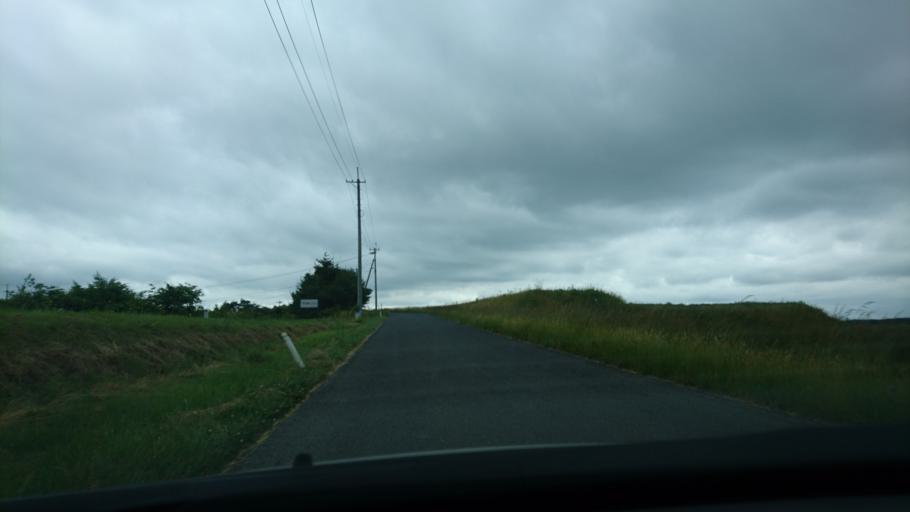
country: JP
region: Iwate
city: Ichinoseki
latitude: 38.8845
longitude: 141.1960
